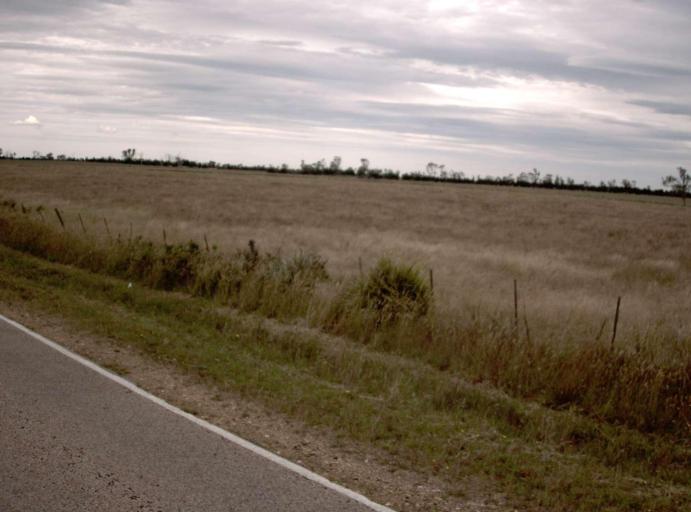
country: AU
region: Victoria
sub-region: East Gippsland
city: Bairnsdale
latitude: -37.9465
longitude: 147.5248
